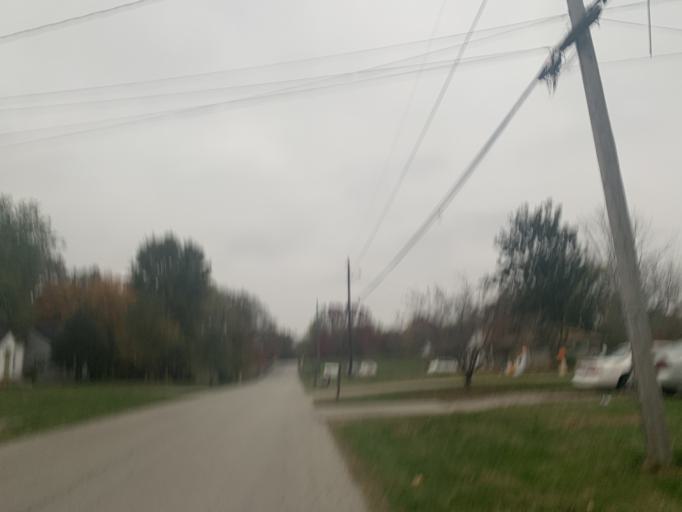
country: US
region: Kentucky
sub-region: Jefferson County
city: Saint Dennis
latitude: 38.2064
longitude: -85.8549
